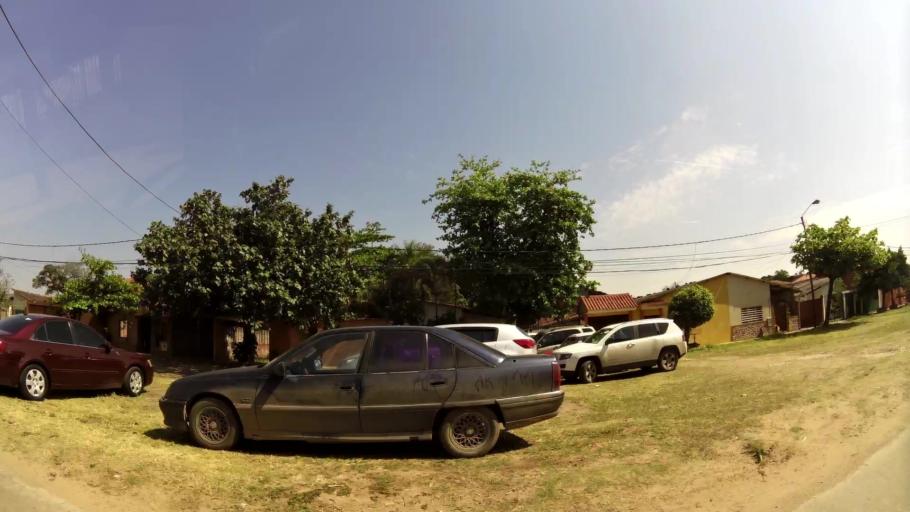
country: BO
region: Santa Cruz
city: Santa Cruz de la Sierra
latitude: -17.7433
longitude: -63.1712
